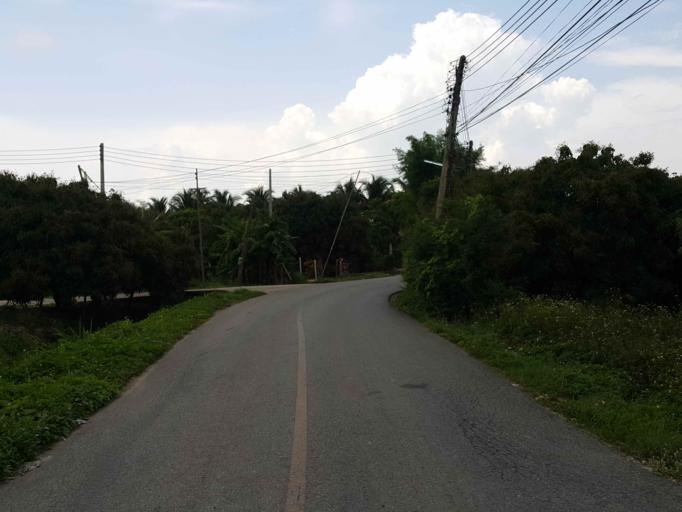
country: TH
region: Chiang Mai
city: Saraphi
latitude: 18.6985
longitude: 99.0281
